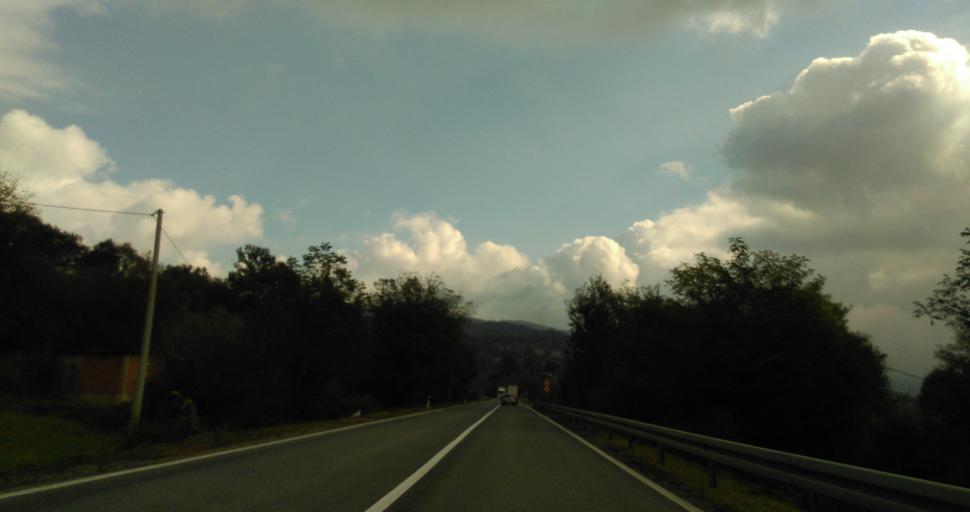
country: RS
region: Central Serbia
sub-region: Kolubarski Okrug
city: Ljig
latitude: 44.1881
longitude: 20.3258
